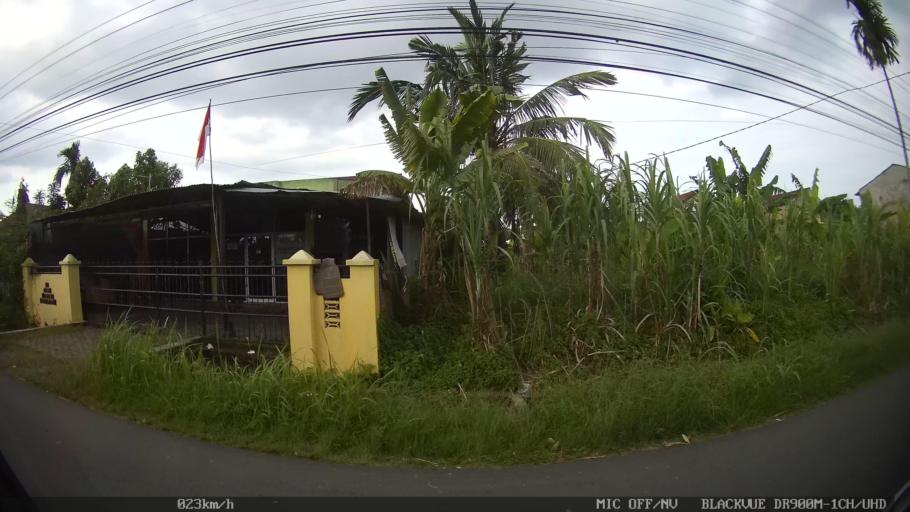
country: ID
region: North Sumatra
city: Sunggal
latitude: 3.5237
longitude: 98.6152
